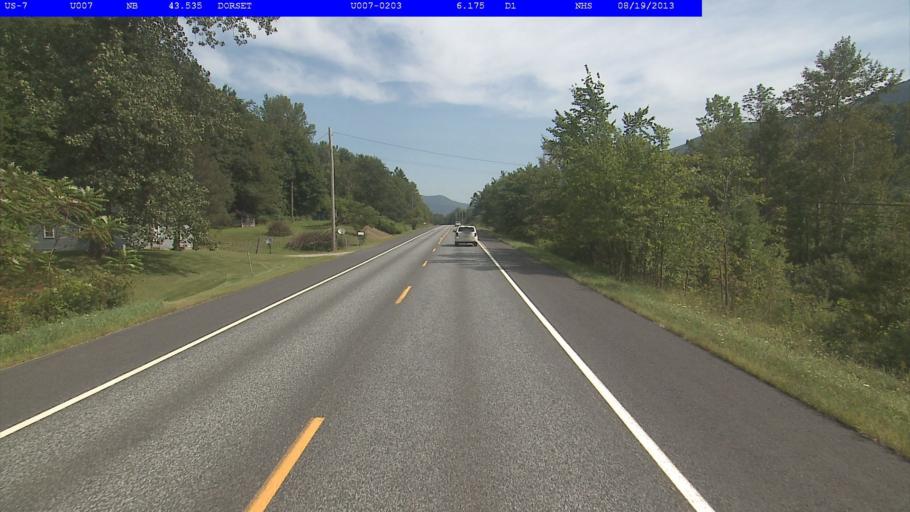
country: US
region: Vermont
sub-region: Bennington County
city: Manchester Center
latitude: 43.2973
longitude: -72.9971
